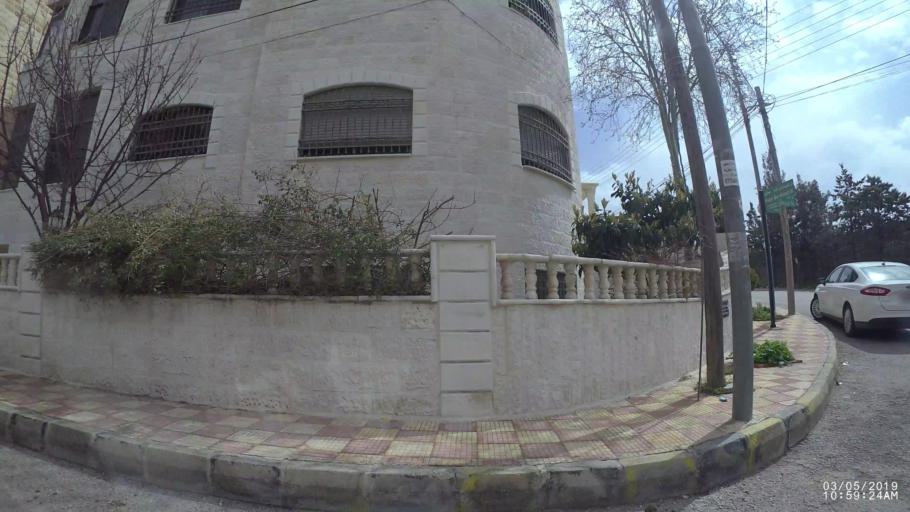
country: JO
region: Amman
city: Amman
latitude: 31.9870
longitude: 35.9216
